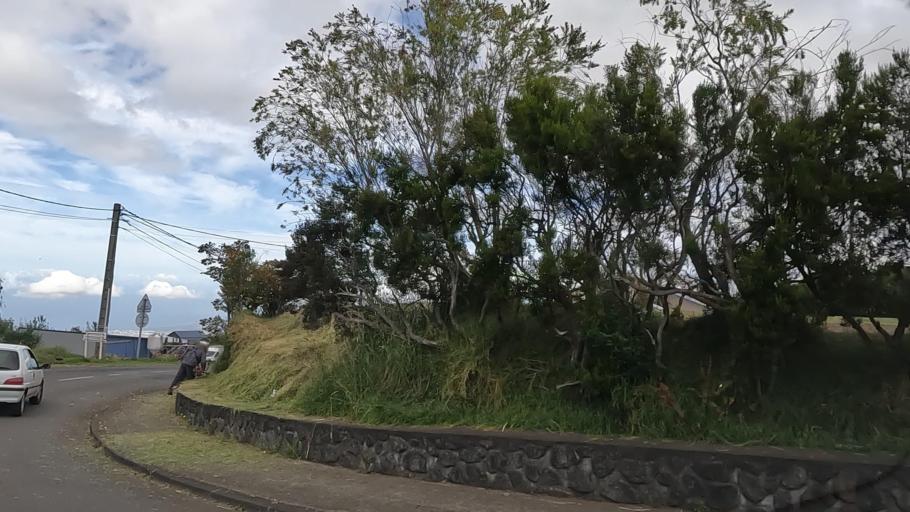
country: RE
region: Reunion
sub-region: Reunion
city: Le Tampon
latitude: -21.2461
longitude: 55.5937
